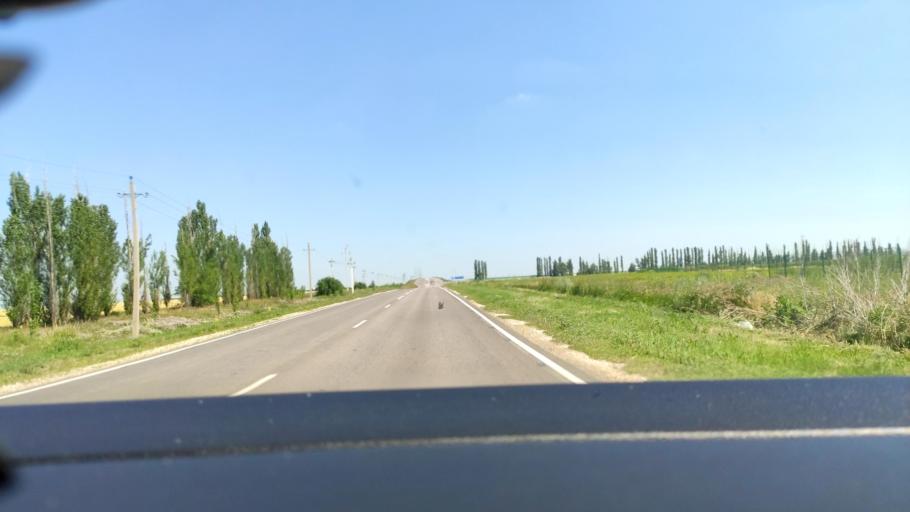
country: RU
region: Voronezj
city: Novaya Usman'
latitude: 51.5826
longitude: 39.3747
